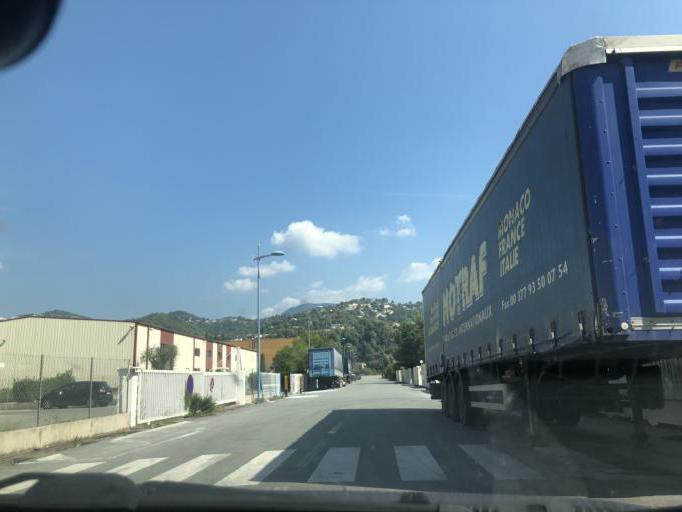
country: FR
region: Provence-Alpes-Cote d'Azur
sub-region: Departement des Alpes-Maritimes
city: Saint-Martin-du-Var
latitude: 43.8051
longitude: 7.1885
